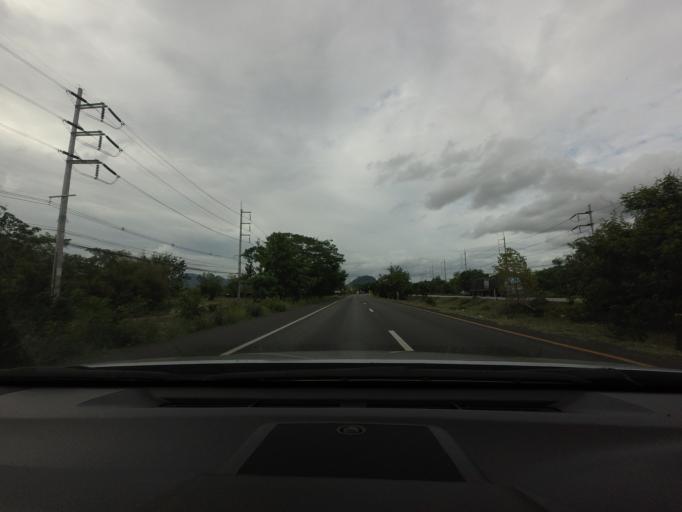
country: TH
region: Prachuap Khiri Khan
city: Hua Hin
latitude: 12.6732
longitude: 99.8807
